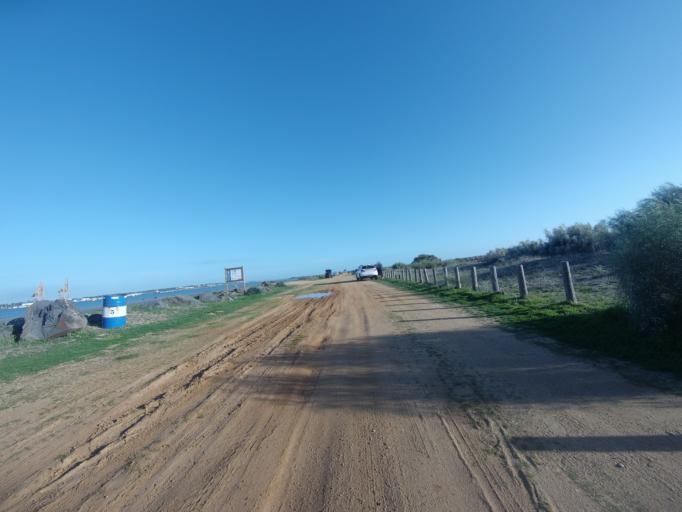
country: ES
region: Andalusia
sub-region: Provincia de Huelva
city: Punta Umbria
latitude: 37.1483
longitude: -6.8936
